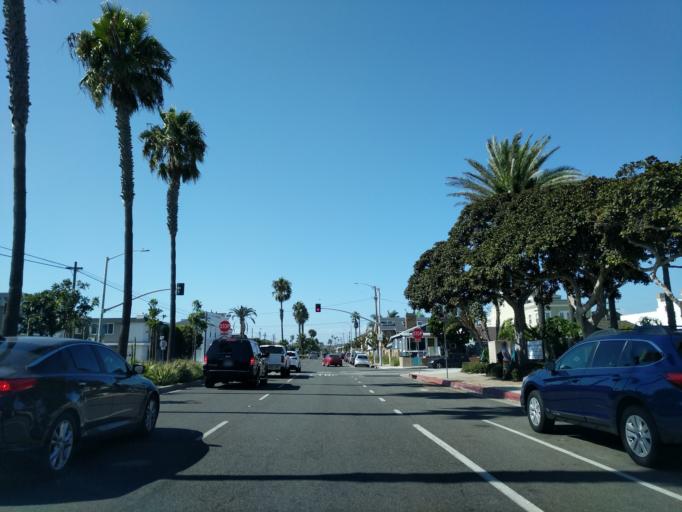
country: US
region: California
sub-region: Orange County
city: Newport Beach
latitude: 33.6175
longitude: -117.9349
